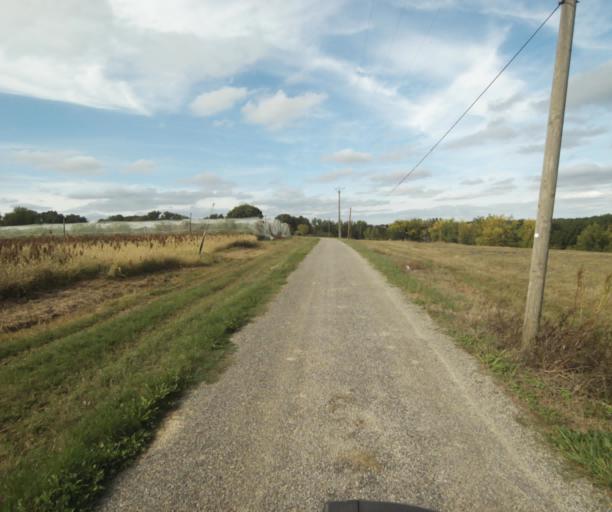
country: FR
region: Midi-Pyrenees
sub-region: Departement du Tarn-et-Garonne
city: Saint-Porquier
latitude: 43.9489
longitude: 1.1328
